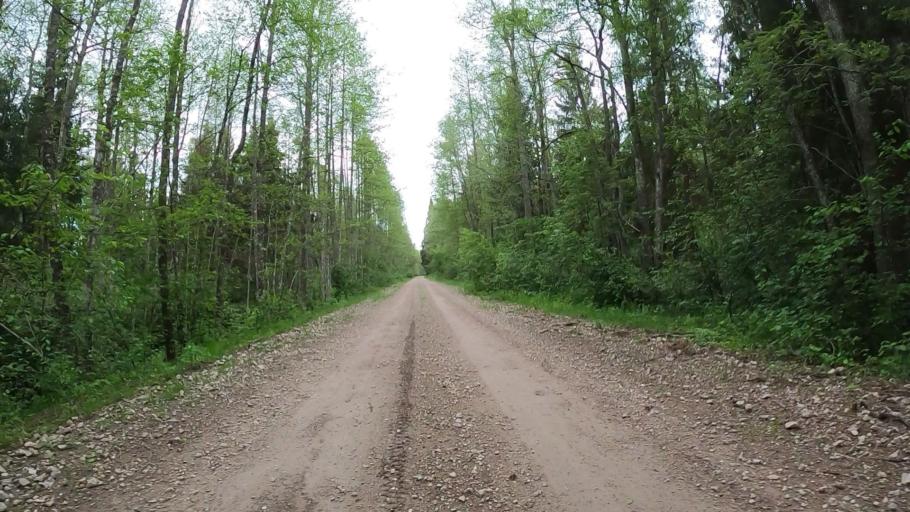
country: LV
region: Ozolnieku
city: Ozolnieki
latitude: 56.8035
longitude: 23.7849
